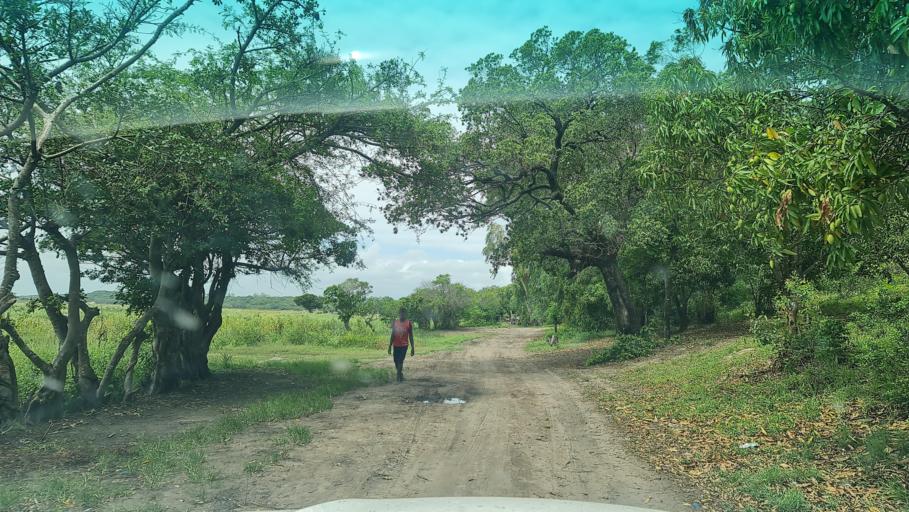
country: MZ
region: Maputo
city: Manhica
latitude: -25.5195
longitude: 32.8649
